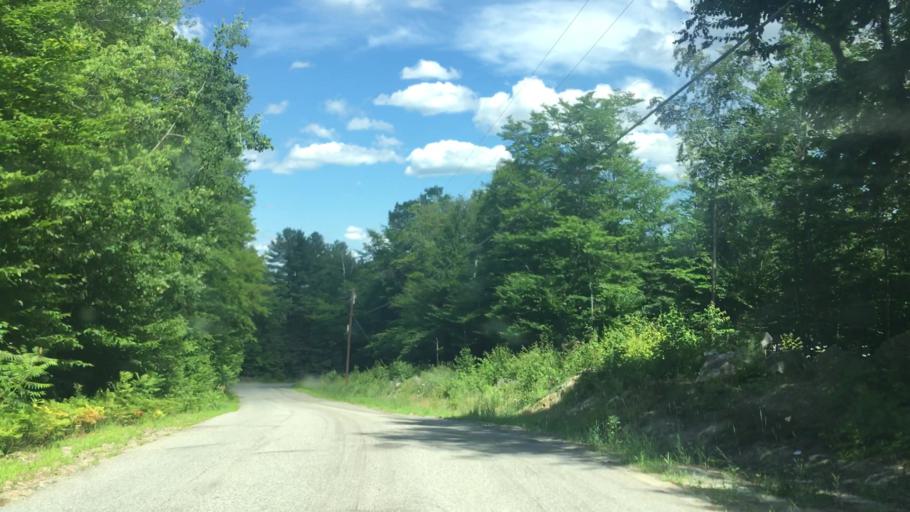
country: US
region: Maine
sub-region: Franklin County
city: Chesterville
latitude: 44.5620
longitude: -70.1355
